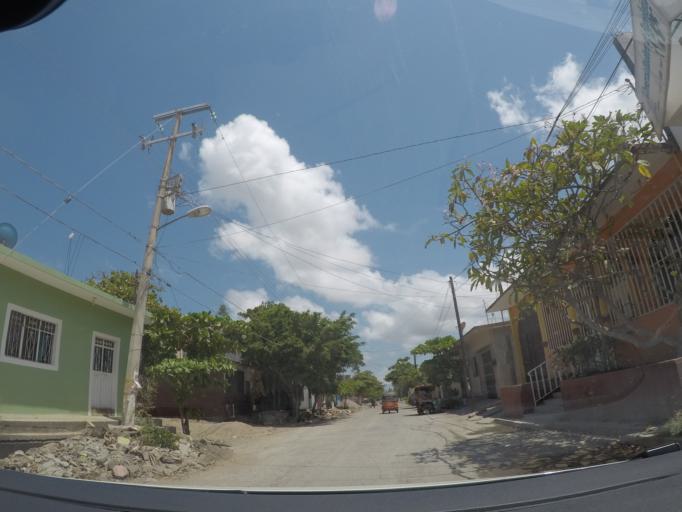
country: MX
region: Oaxaca
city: Juchitan de Zaragoza
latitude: 16.4348
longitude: -95.0159
